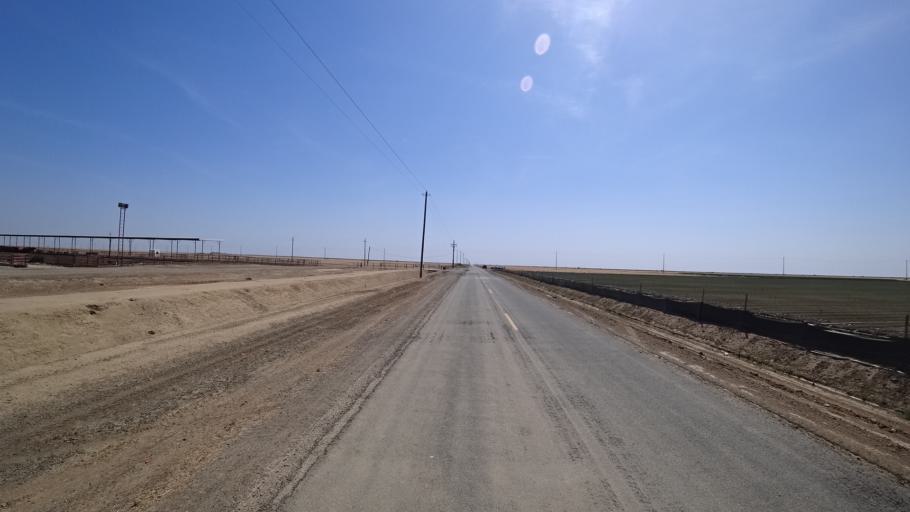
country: US
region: California
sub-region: Kings County
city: Kettleman City
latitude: 36.0941
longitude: -119.9338
